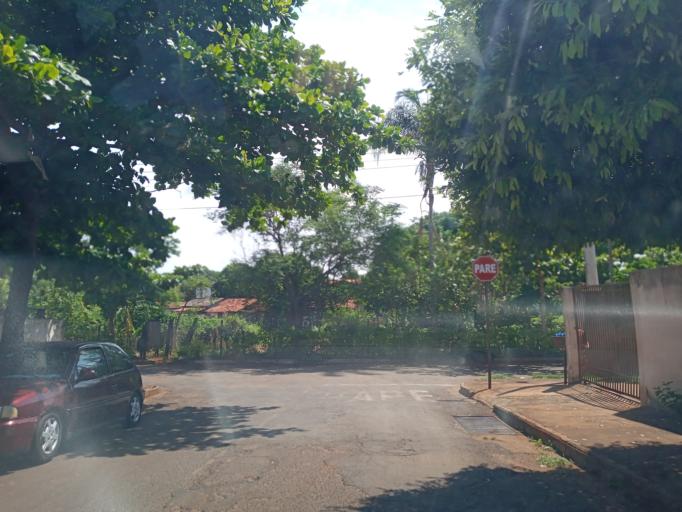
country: BR
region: Minas Gerais
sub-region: Ituiutaba
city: Ituiutaba
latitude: -18.9959
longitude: -49.4732
